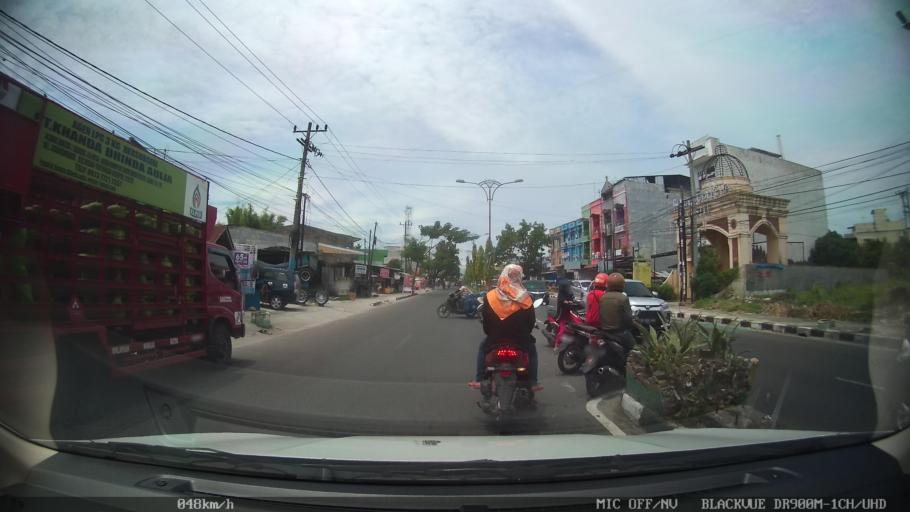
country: ID
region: North Sumatra
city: Sunggal
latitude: 3.5496
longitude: 98.6288
